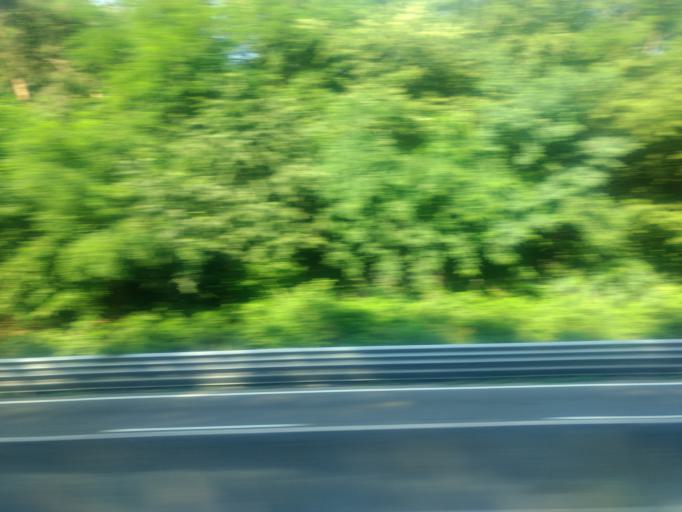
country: IT
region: Lombardy
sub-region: Provincia di Varese
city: Casorate Sempione
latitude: 45.6485
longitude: 8.7465
